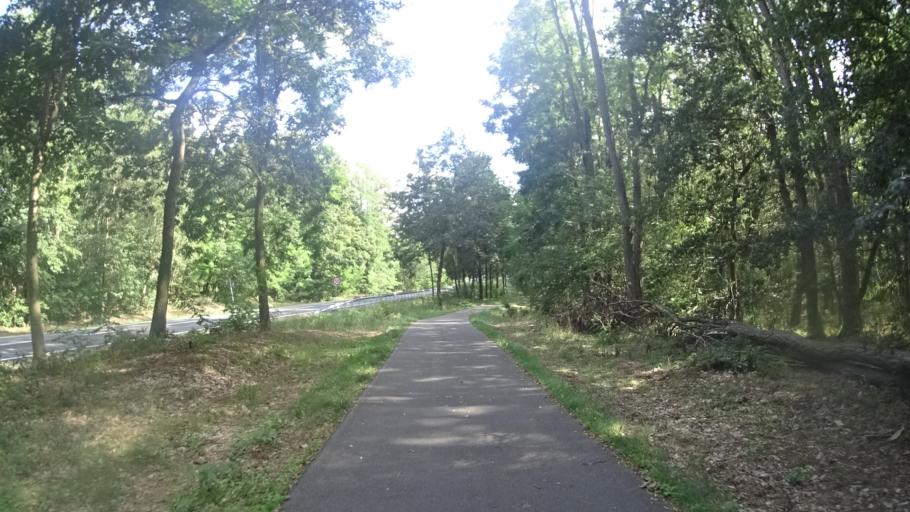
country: DE
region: Brandenburg
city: Rhinow
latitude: 52.7185
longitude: 12.3646
